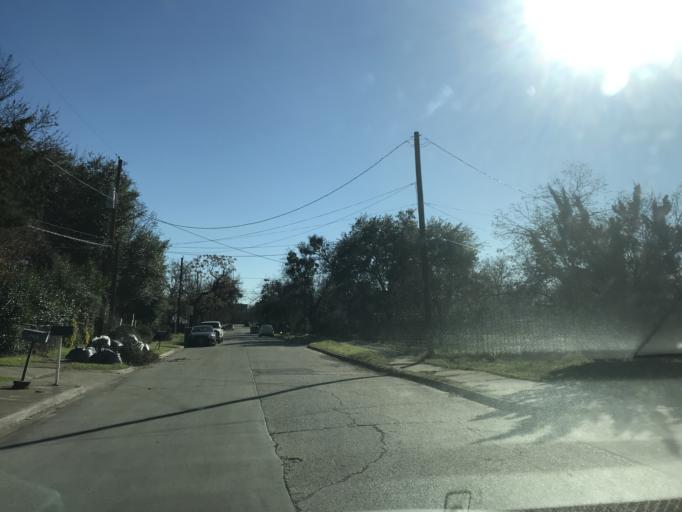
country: US
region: Texas
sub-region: Dallas County
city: Cockrell Hill
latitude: 32.7721
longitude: -96.9096
